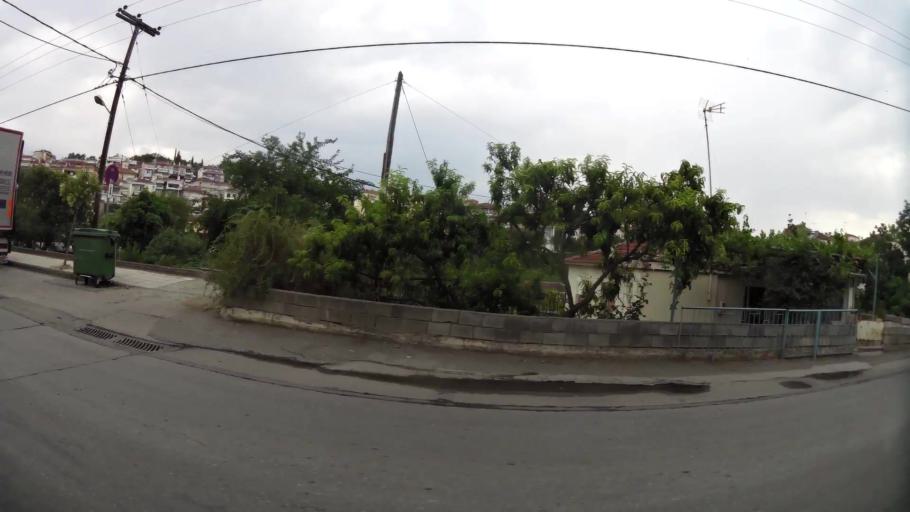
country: GR
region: Central Macedonia
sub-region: Nomos Imathias
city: Veroia
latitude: 40.5257
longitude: 22.1978
